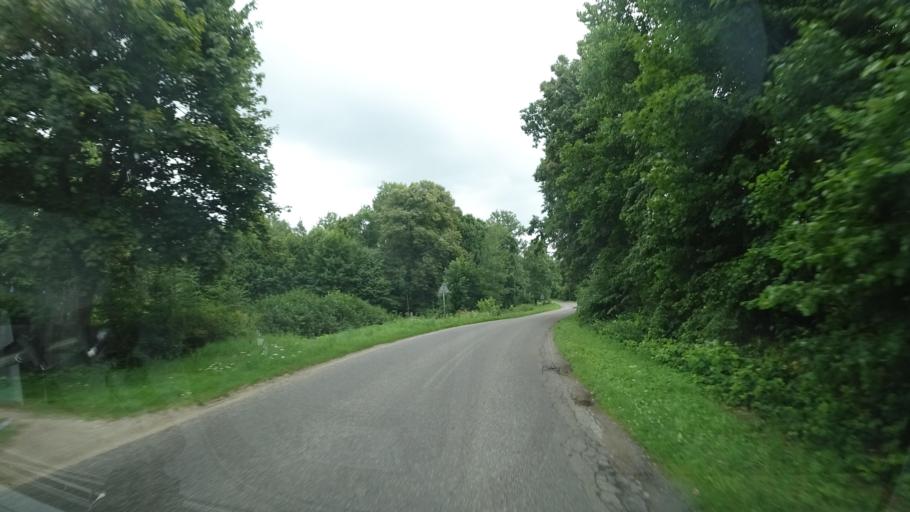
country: PL
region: Warmian-Masurian Voivodeship
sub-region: Powiat goldapski
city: Goldap
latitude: 54.3111
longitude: 22.3718
